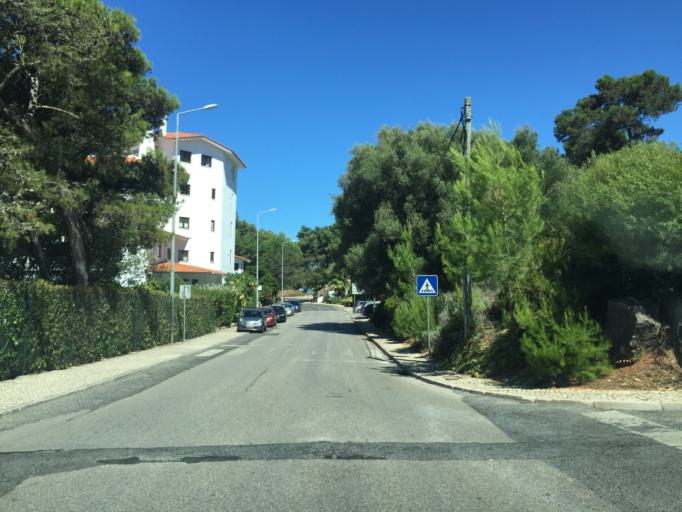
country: PT
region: Lisbon
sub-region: Cascais
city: Cascais
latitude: 38.7033
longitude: -9.4331
